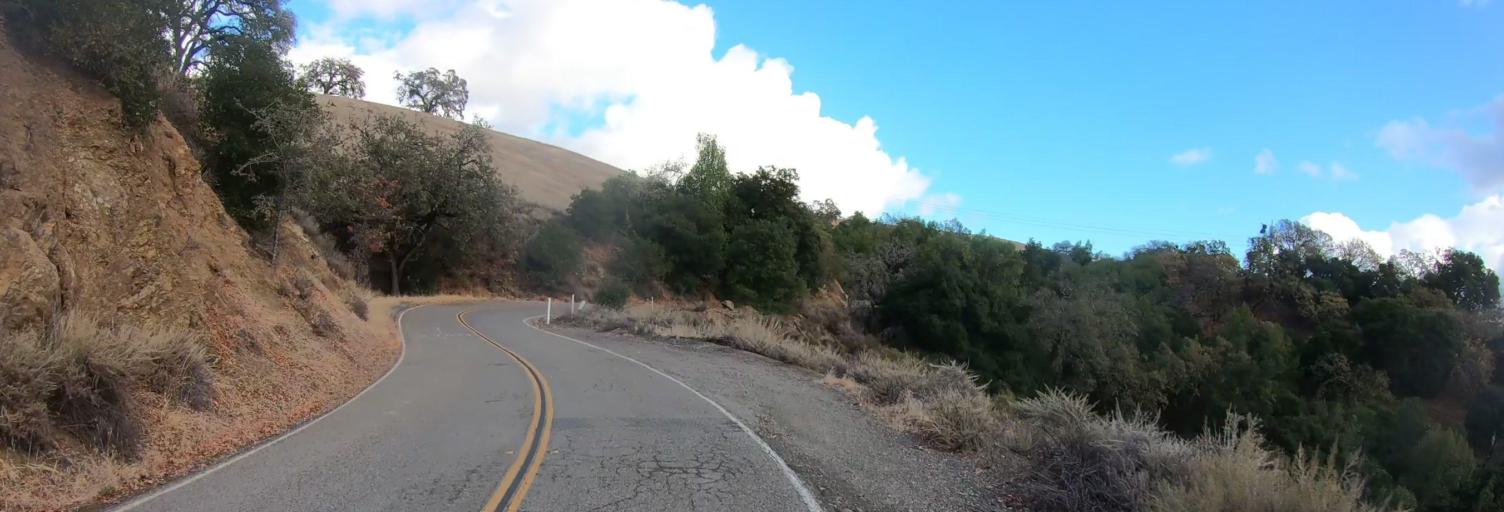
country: US
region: California
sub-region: Santa Clara County
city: East Foothills
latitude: 37.3318
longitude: -121.6878
